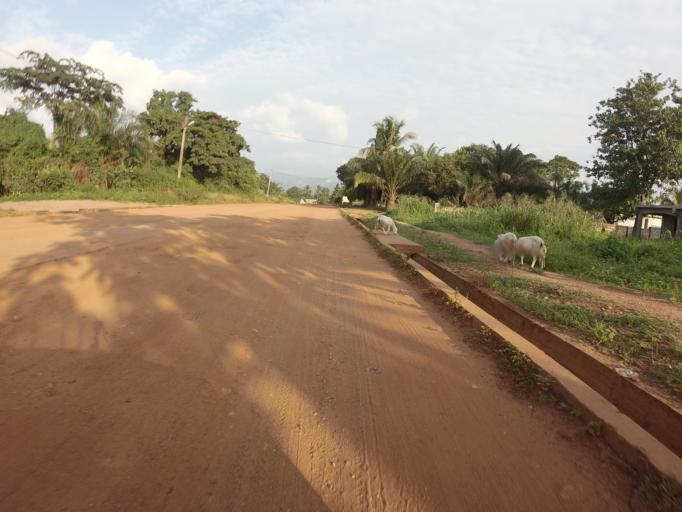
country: GH
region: Volta
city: Kpandu
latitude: 6.9669
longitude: 0.4559
